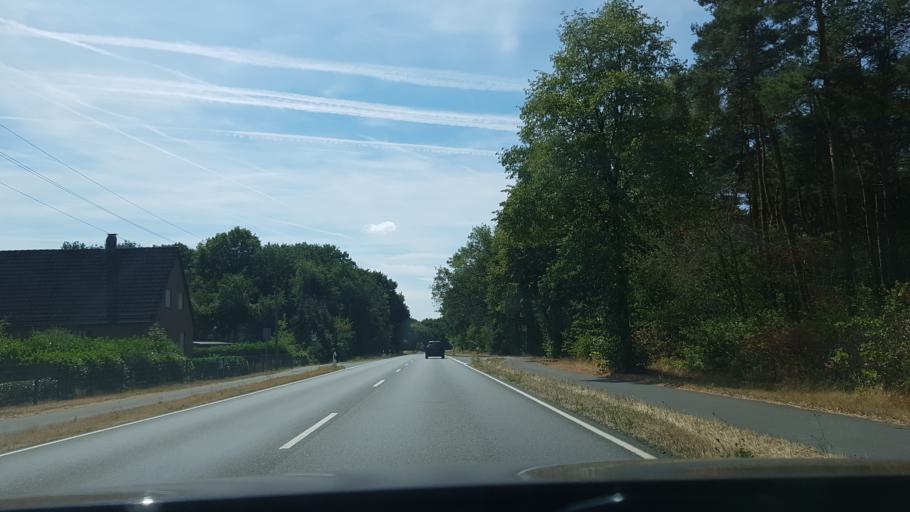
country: DE
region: North Rhine-Westphalia
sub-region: Regierungsbezirk Dusseldorf
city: Voerde
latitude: 51.6244
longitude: 6.7042
